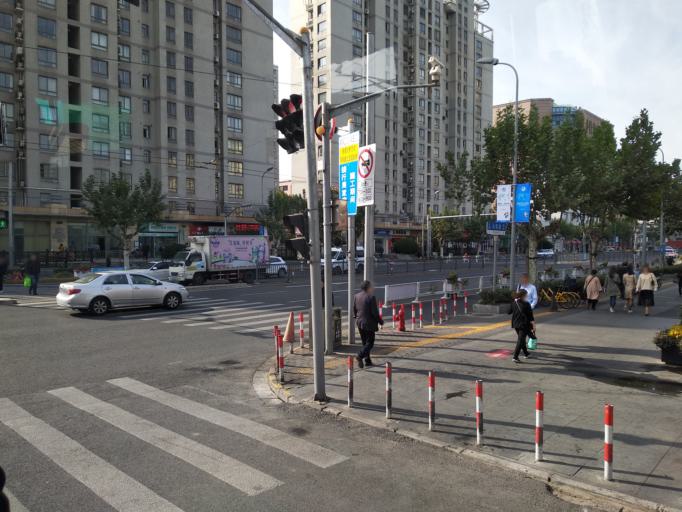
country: CN
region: Shanghai Shi
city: Yangpu
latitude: 31.2726
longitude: 121.5311
